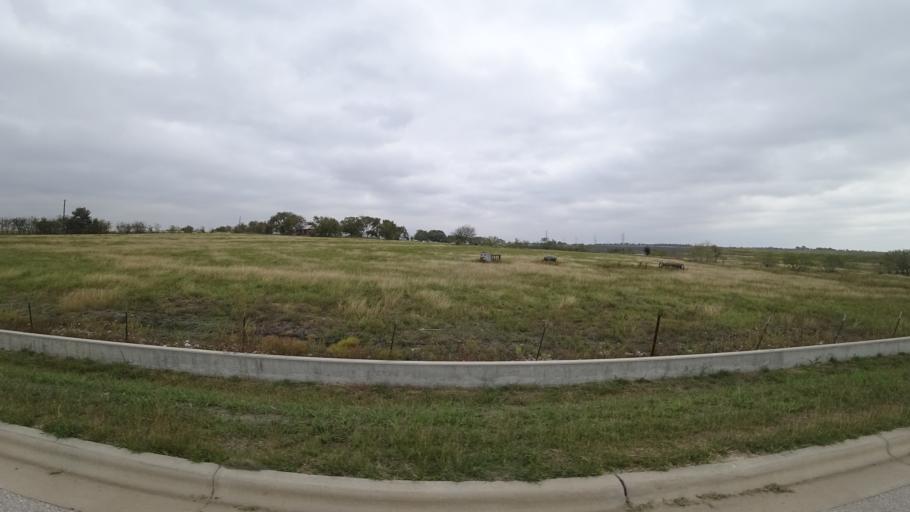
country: US
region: Texas
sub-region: Travis County
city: Pflugerville
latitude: 30.4025
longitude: -97.5765
